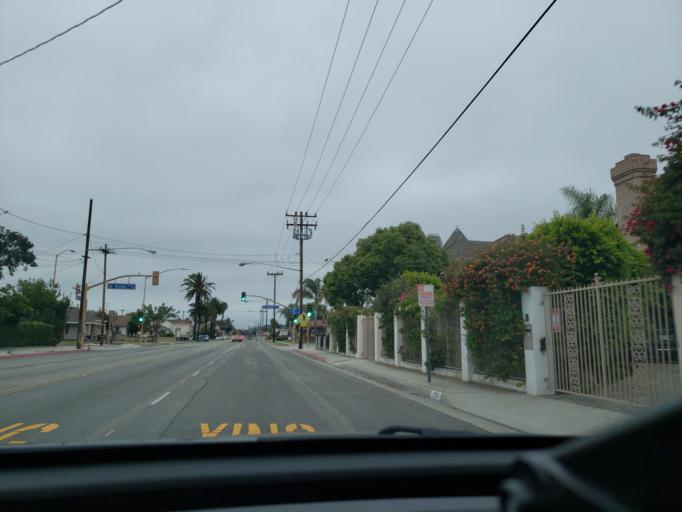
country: US
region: California
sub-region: Los Angeles County
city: Artesia
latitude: 33.8657
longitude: -118.0873
